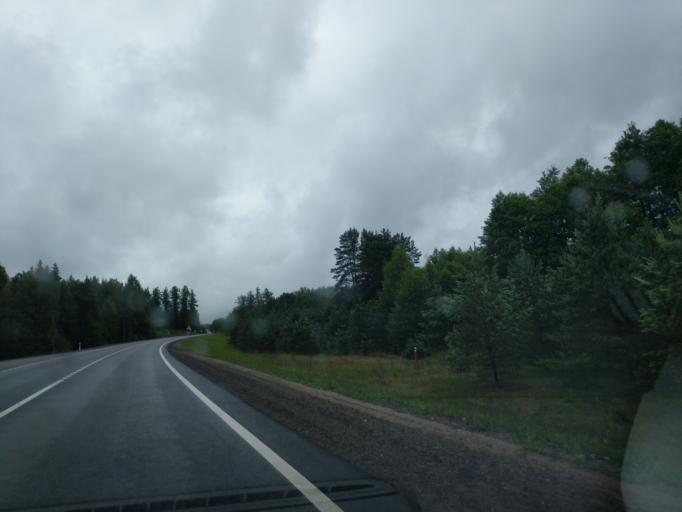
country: BY
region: Minsk
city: Syomkava
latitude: 54.2302
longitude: 27.4843
